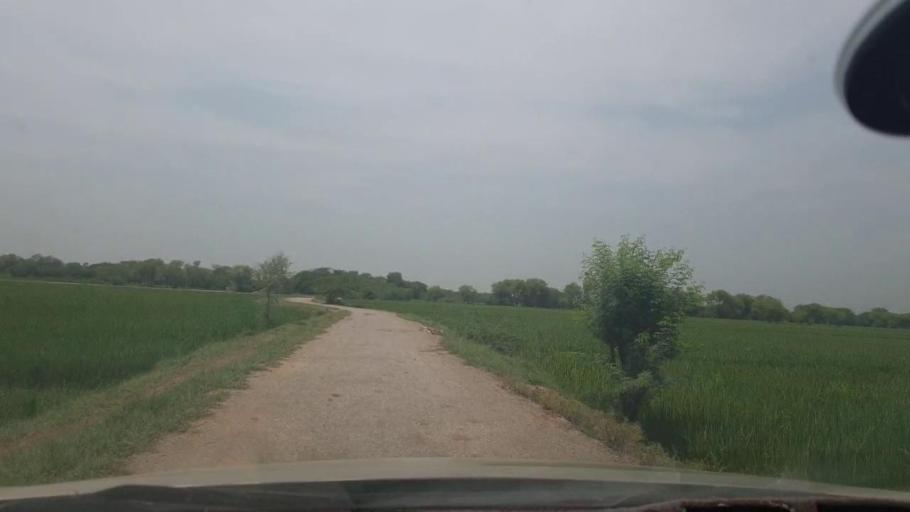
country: PK
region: Sindh
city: Jacobabad
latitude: 28.2411
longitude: 68.4211
